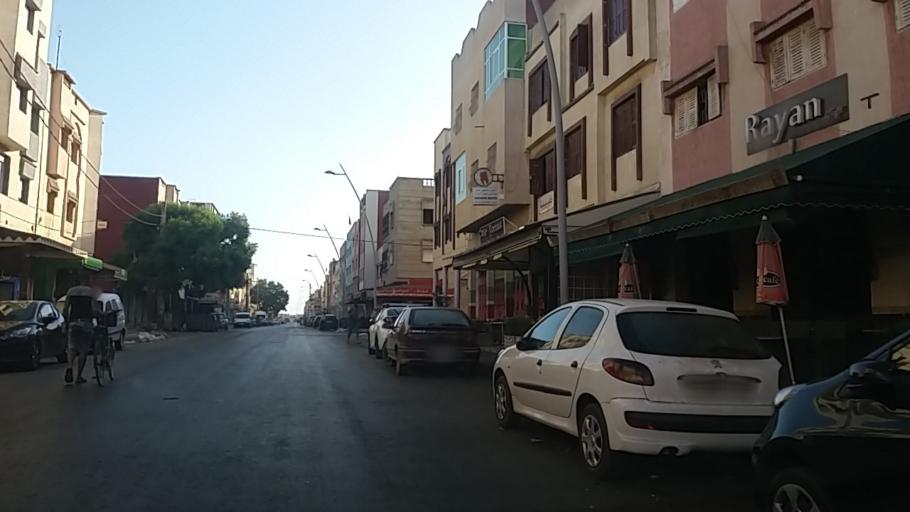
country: MA
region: Gharb-Chrarda-Beni Hssen
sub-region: Kenitra Province
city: Kenitra
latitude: 34.2568
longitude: -6.6223
